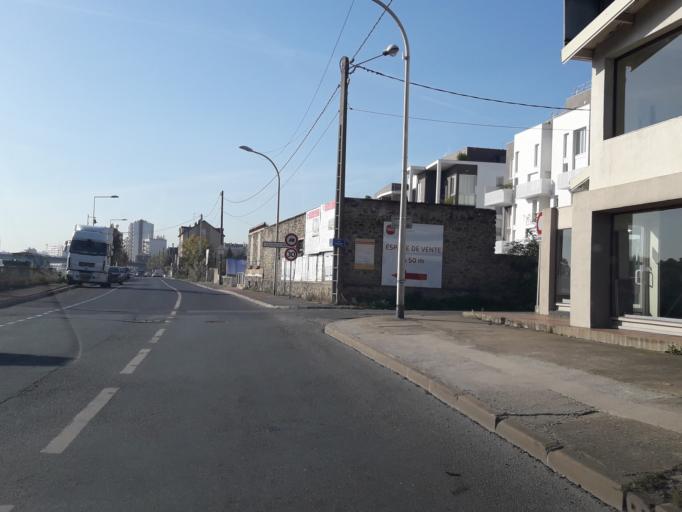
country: FR
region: Ile-de-France
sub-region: Departement de l'Essonne
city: Juvisy-sur-Orge
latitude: 48.6928
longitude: 2.3894
